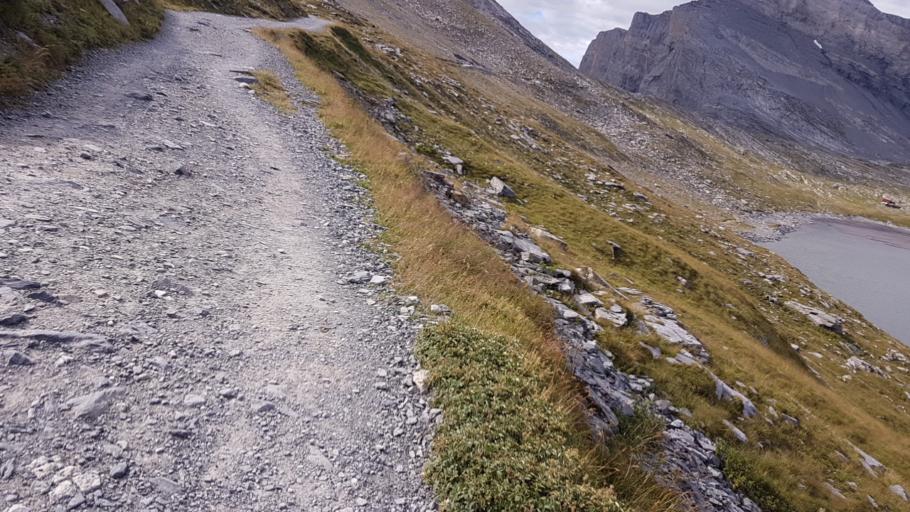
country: CH
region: Valais
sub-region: Leuk District
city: Leukerbad
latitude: 46.4093
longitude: 7.6220
